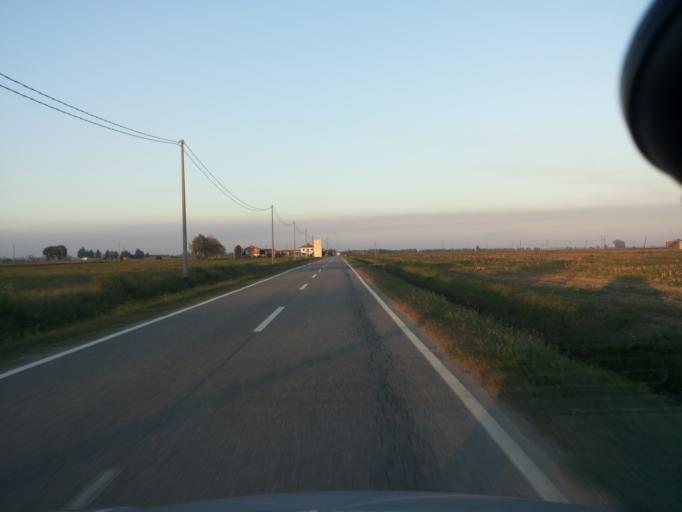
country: IT
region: Piedmont
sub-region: Provincia di Vercelli
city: Santhia
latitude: 45.3774
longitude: 8.2004
